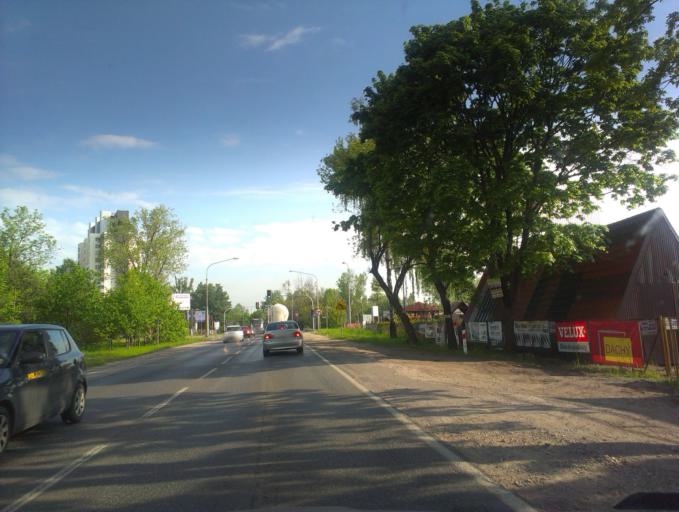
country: PL
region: Masovian Voivodeship
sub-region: Powiat piaseczynski
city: Piaseczno
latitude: 52.0756
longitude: 21.0355
